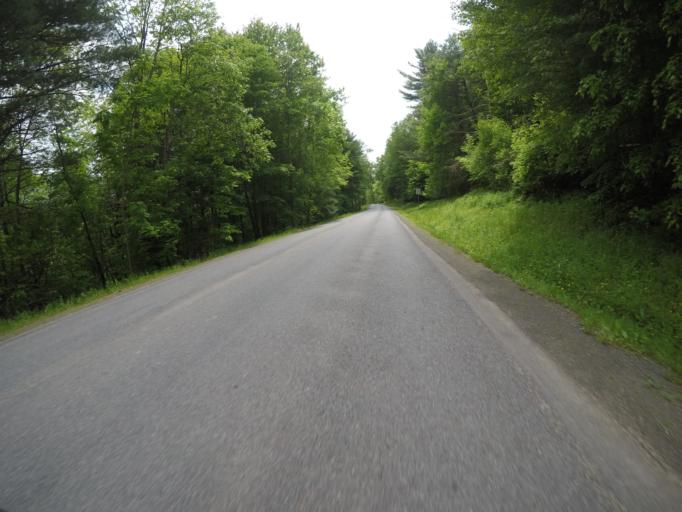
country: US
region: New York
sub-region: Delaware County
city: Stamford
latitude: 42.2171
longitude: -74.6828
